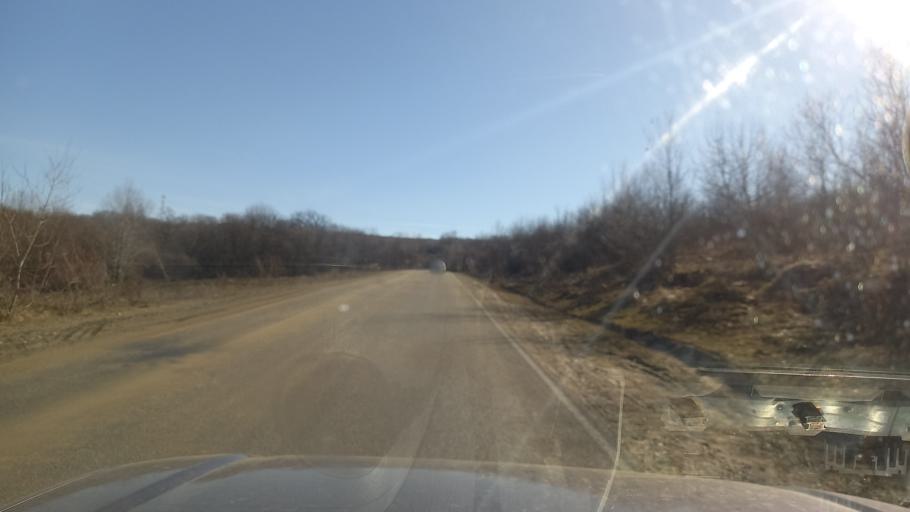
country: RU
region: Adygeya
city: Kamennomostskiy
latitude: 44.2795
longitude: 40.2137
